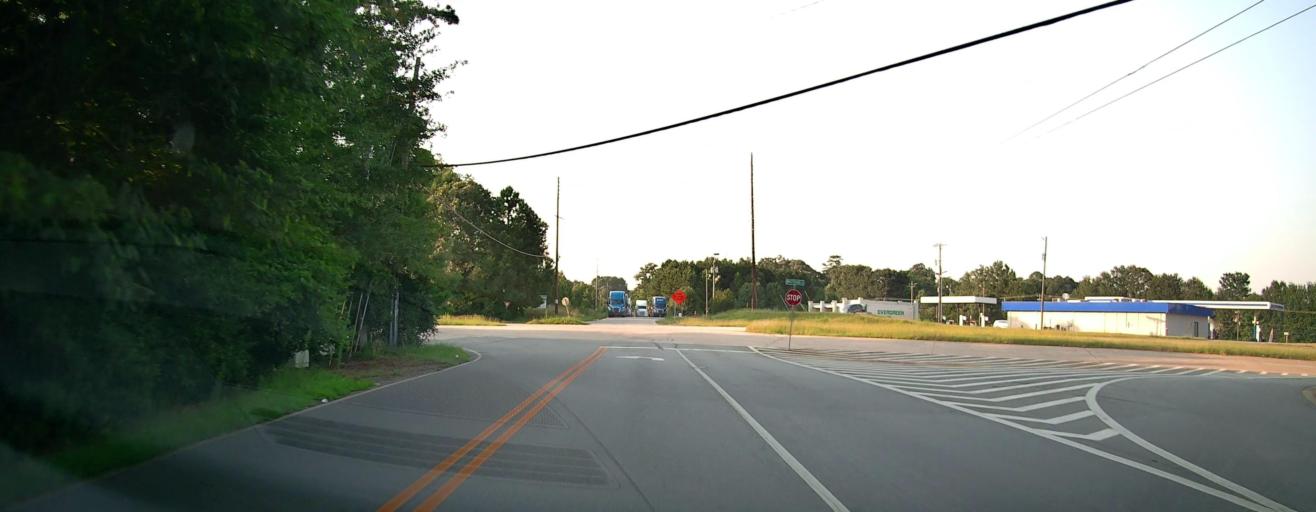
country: US
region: Georgia
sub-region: Bibb County
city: Macon
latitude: 32.9316
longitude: -83.7167
